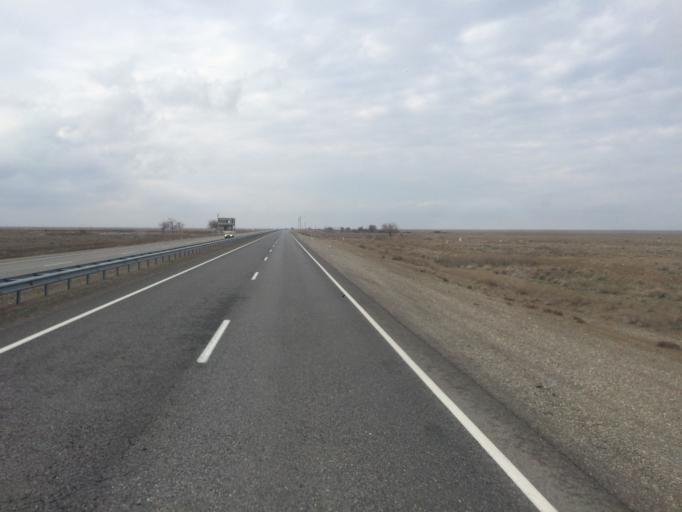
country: KZ
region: Ongtustik Qazaqstan
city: Turkestan
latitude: 43.5251
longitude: 67.7951
